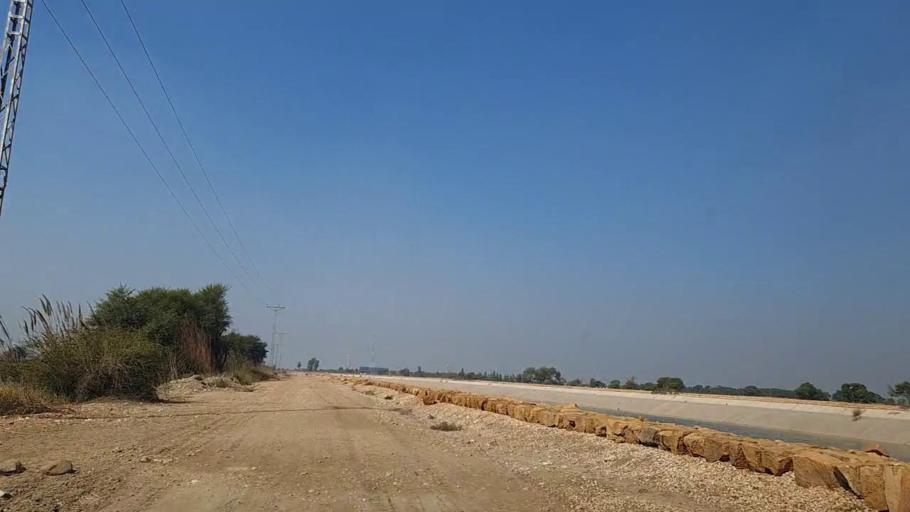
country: PK
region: Sindh
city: Sakrand
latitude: 26.2395
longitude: 68.2757
